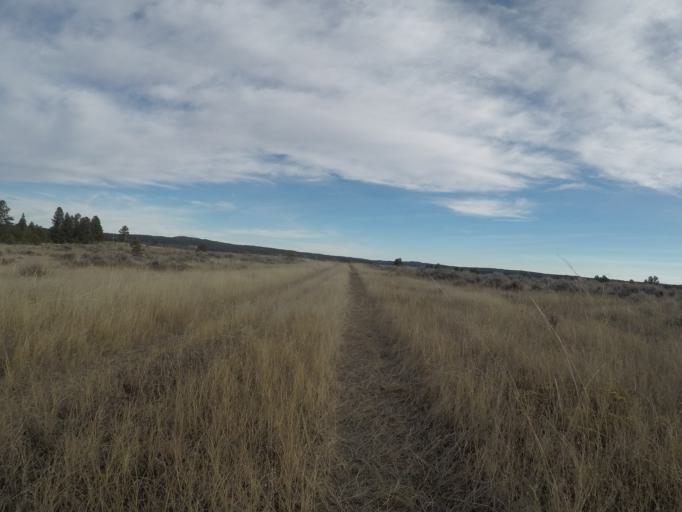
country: US
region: Montana
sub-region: Musselshell County
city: Roundup
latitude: 46.2749
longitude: -108.7499
